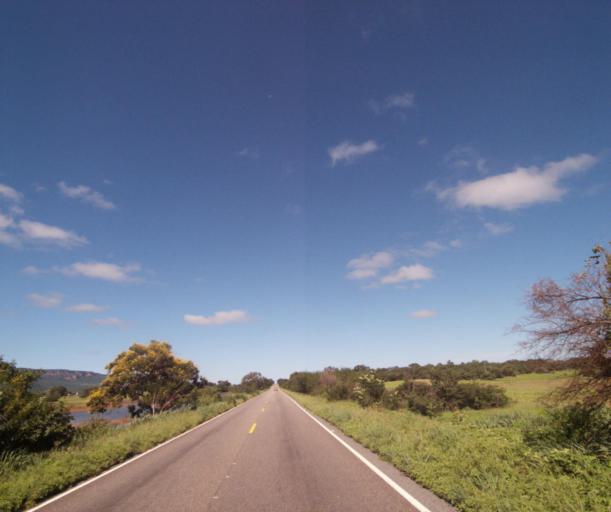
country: BR
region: Bahia
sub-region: Palmas De Monte Alto
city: Palmas de Monte Alto
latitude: -14.2423
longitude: -43.0733
